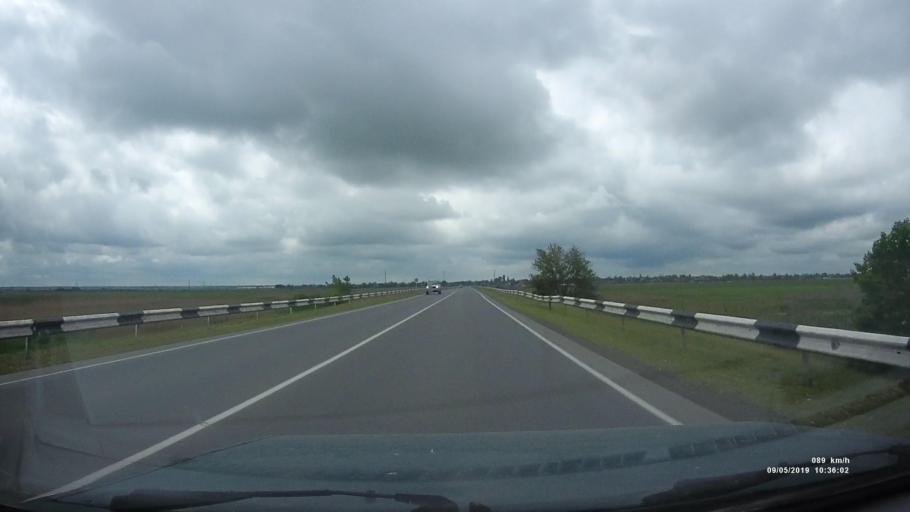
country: RU
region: Rostov
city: Peshkovo
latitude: 47.0340
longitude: 39.4103
